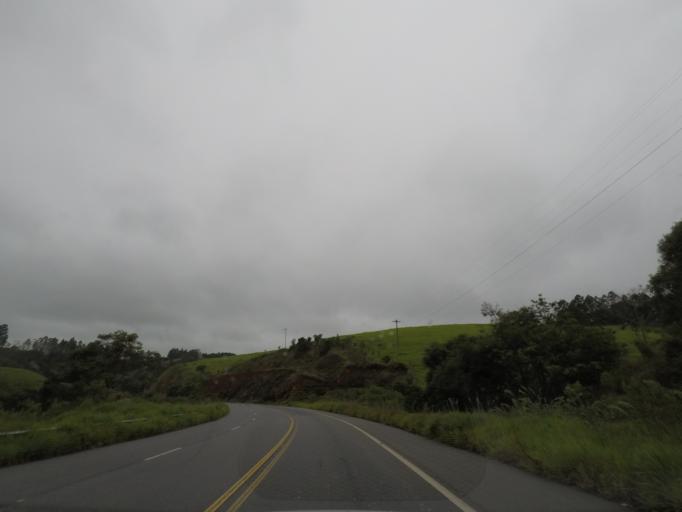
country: BR
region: Sao Paulo
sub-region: Guaratingueta
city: Guaratingueta
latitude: -22.9378
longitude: -45.0688
